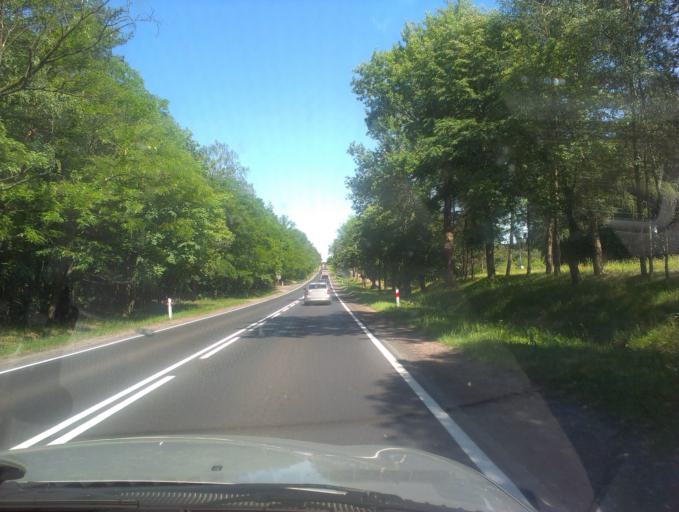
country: PL
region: Pomeranian Voivodeship
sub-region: Powiat czluchowski
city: Czluchow
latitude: 53.6805
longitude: 17.4053
